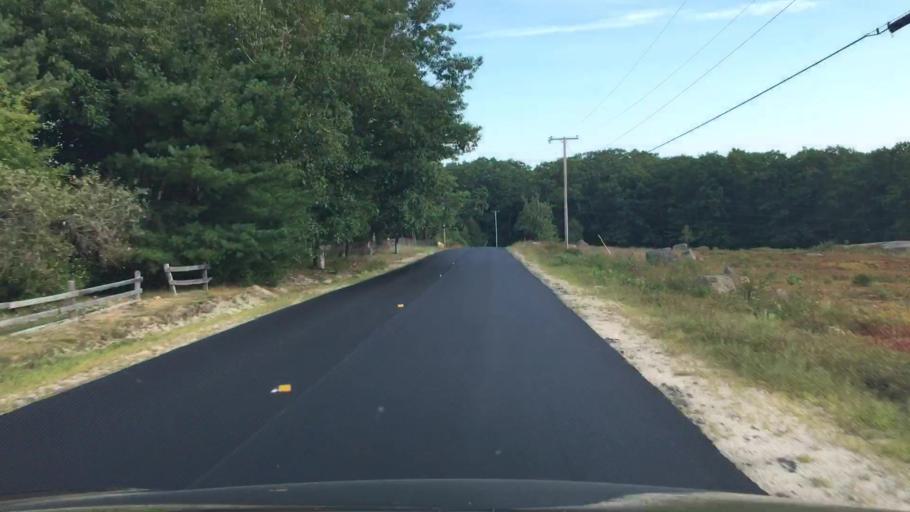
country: US
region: Maine
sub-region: Hancock County
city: Surry
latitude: 44.5270
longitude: -68.6105
